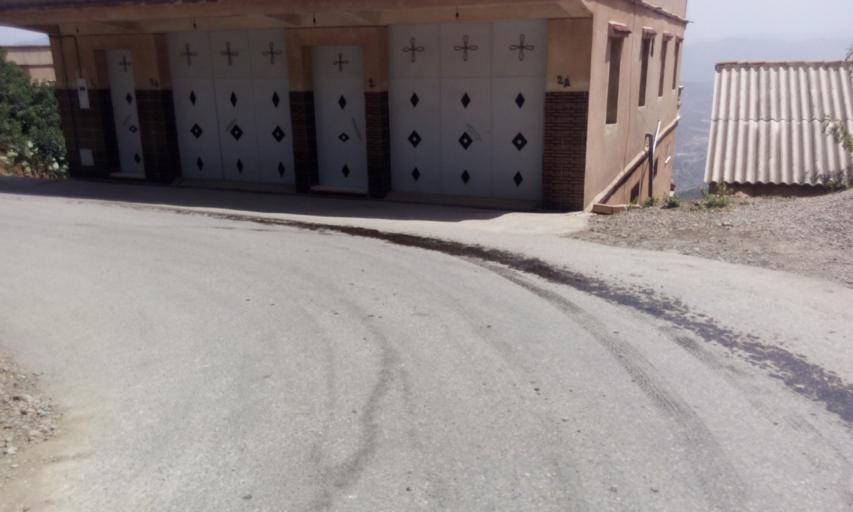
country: DZ
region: Tizi Ouzou
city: Chemini
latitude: 36.6067
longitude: 4.6338
